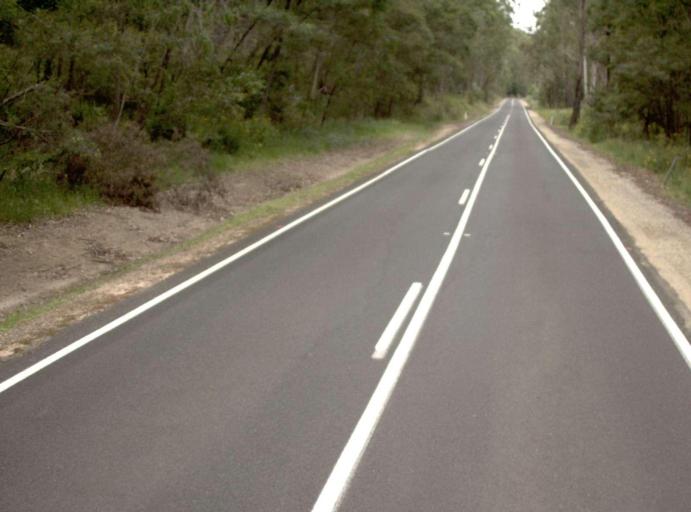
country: AU
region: New South Wales
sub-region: Bombala
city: Bombala
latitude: -37.4458
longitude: 149.1939
